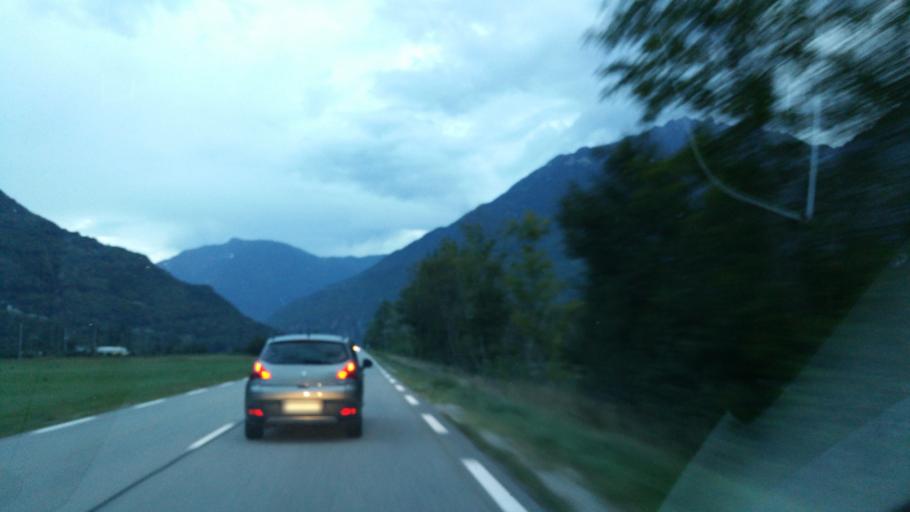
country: FR
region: Rhone-Alpes
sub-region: Departement de la Savoie
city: Saint-Remy-de-Maurienne
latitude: 45.4050
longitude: 6.2749
